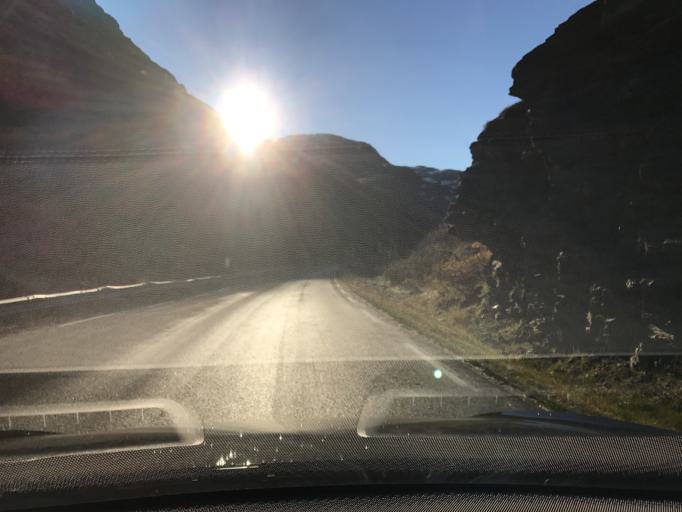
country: NO
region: Sogn og Fjordane
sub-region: Laerdal
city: Laerdalsoyri
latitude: 60.8131
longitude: 7.5544
